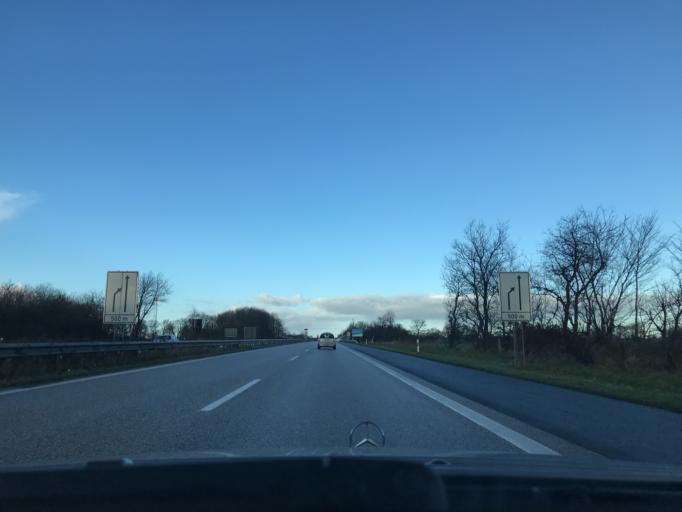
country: DE
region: Schleswig-Holstein
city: Handewitt
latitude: 54.7991
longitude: 9.3317
